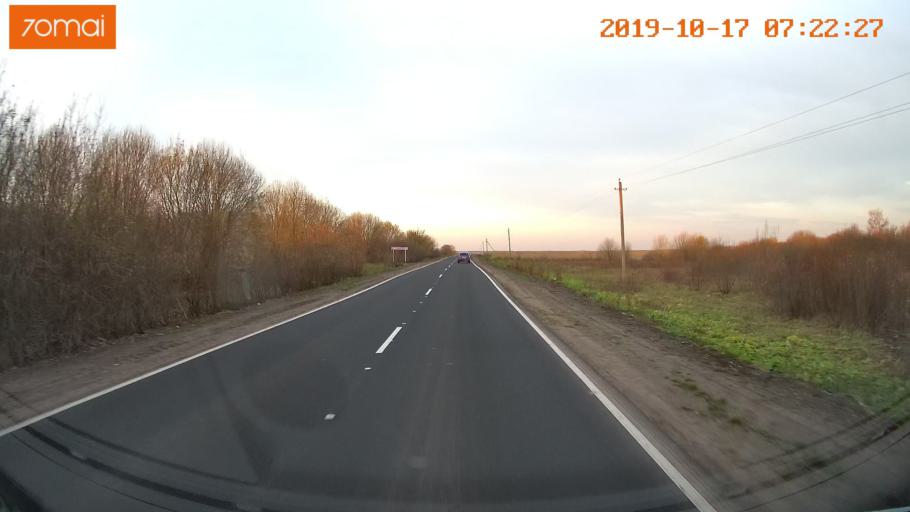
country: RU
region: Ivanovo
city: Gavrilov Posad
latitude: 56.3431
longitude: 40.1397
